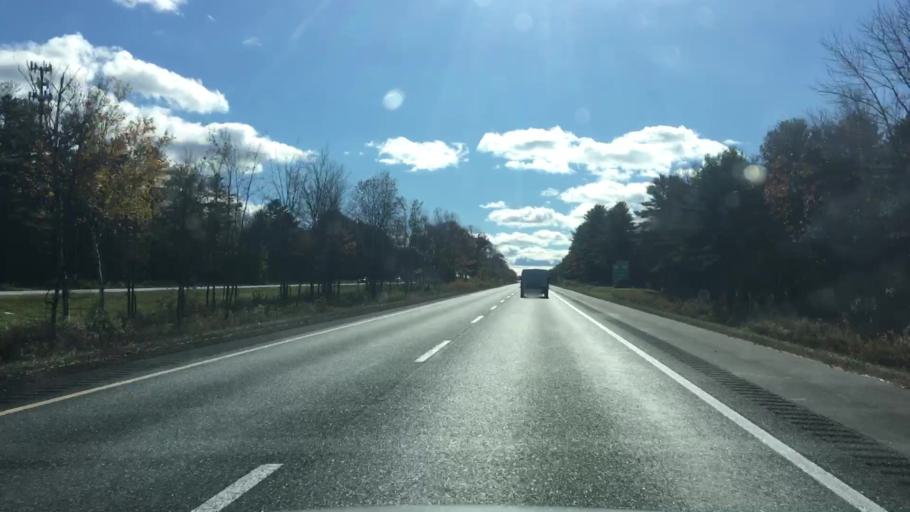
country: US
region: Maine
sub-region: Kennebec County
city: Waterville
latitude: 44.5628
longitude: -69.6716
